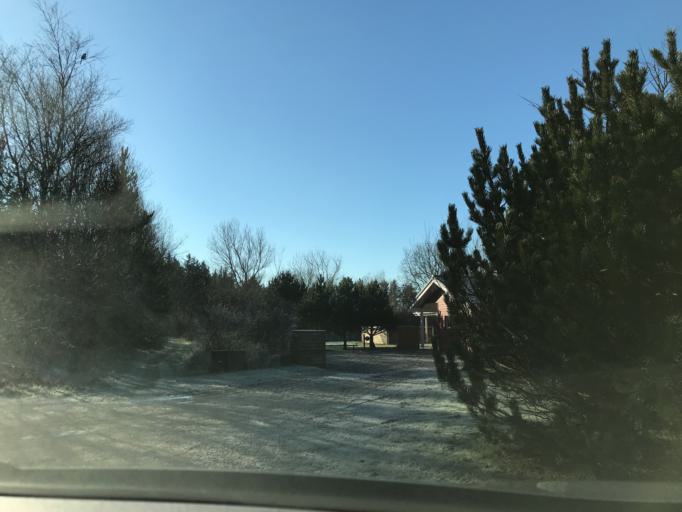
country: DK
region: South Denmark
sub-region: Varde Kommune
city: Oksbol
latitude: 55.7744
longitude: 8.2452
